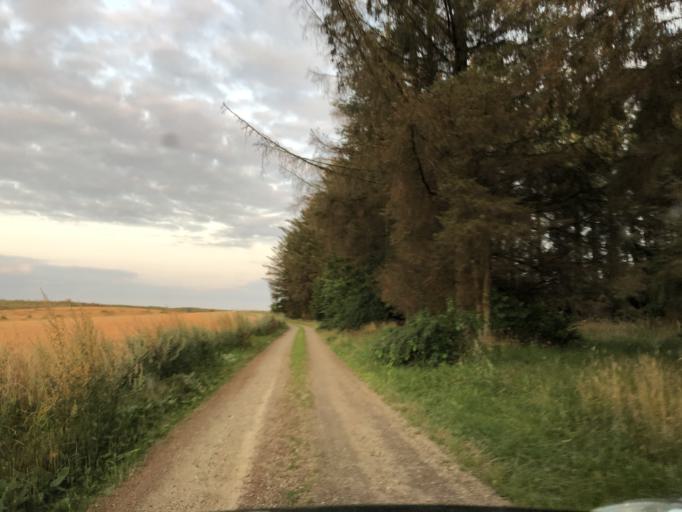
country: DK
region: Central Jutland
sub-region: Holstebro Kommune
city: Vinderup
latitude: 56.4555
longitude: 8.8968
